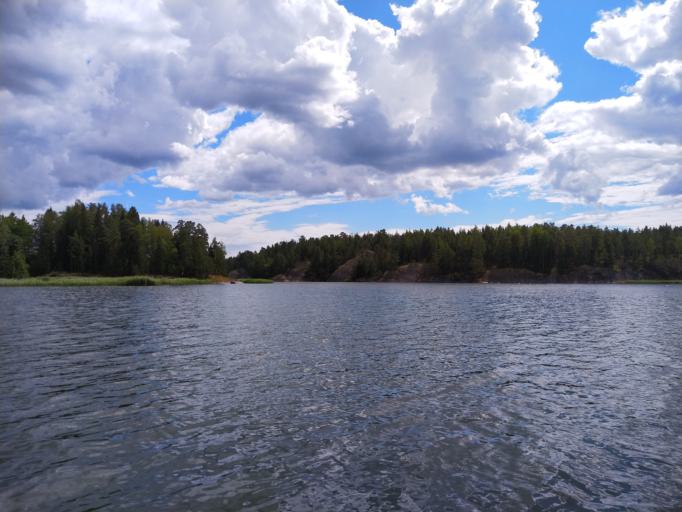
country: FI
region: Uusimaa
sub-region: Raaseporin
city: Karis
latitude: 59.9709
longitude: 23.7028
